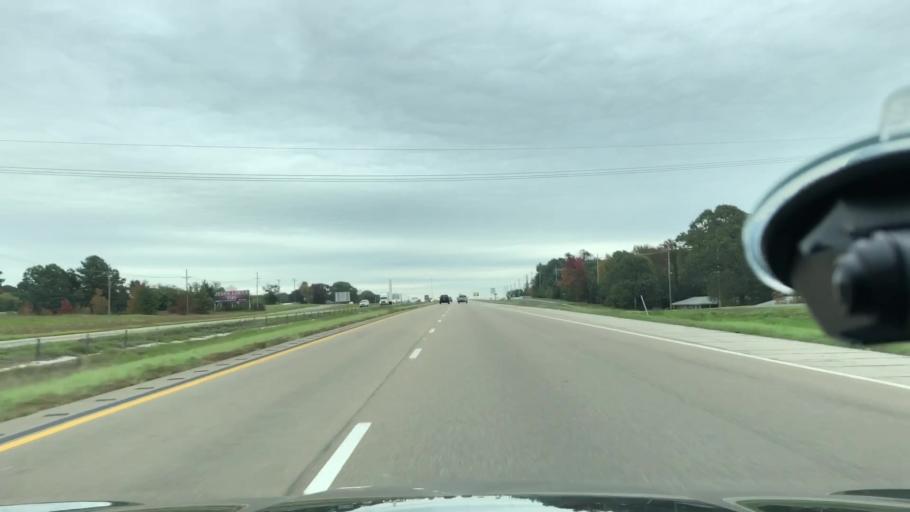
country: US
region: Texas
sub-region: Titus County
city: Mount Pleasant
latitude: 33.1720
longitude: -94.9921
